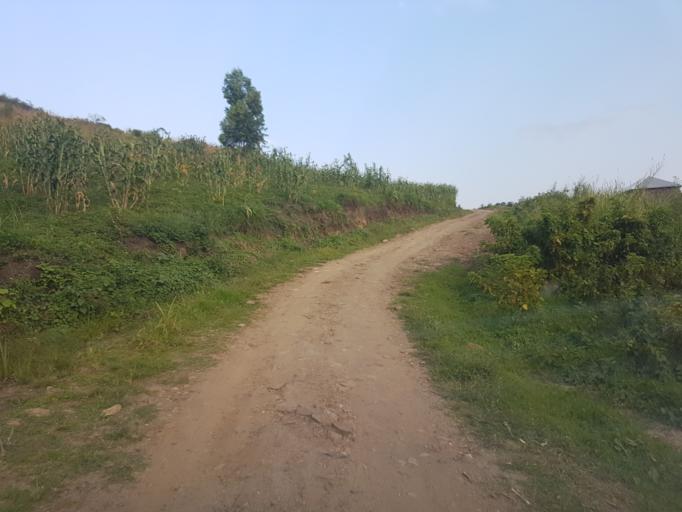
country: UG
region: Western Region
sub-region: Mitoma District
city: Mitoma
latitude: -0.6808
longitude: 29.9088
